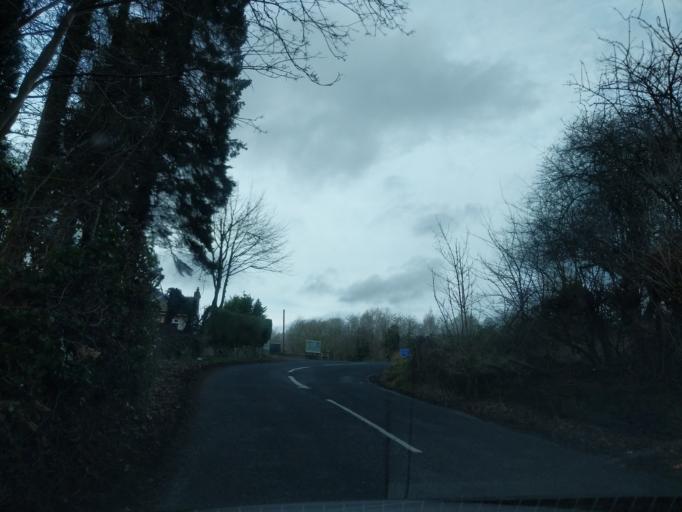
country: GB
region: Scotland
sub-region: South Lanarkshire
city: Carluke
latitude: 55.7008
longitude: -3.8589
